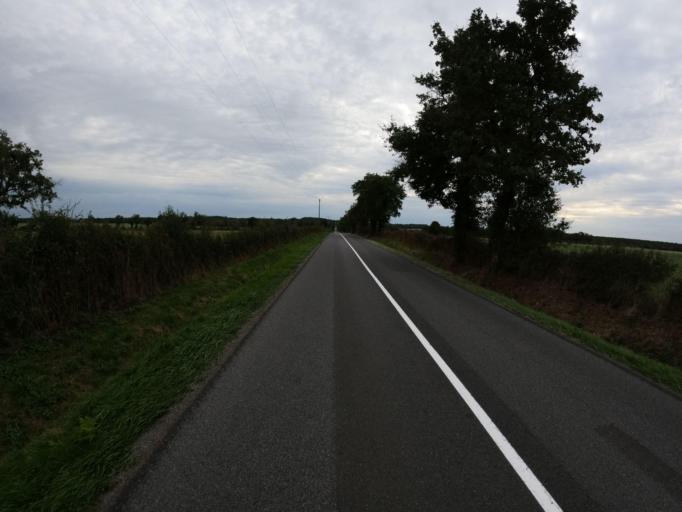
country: FR
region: Poitou-Charentes
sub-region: Departement de la Vienne
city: Saulge
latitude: 46.3647
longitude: 0.8387
